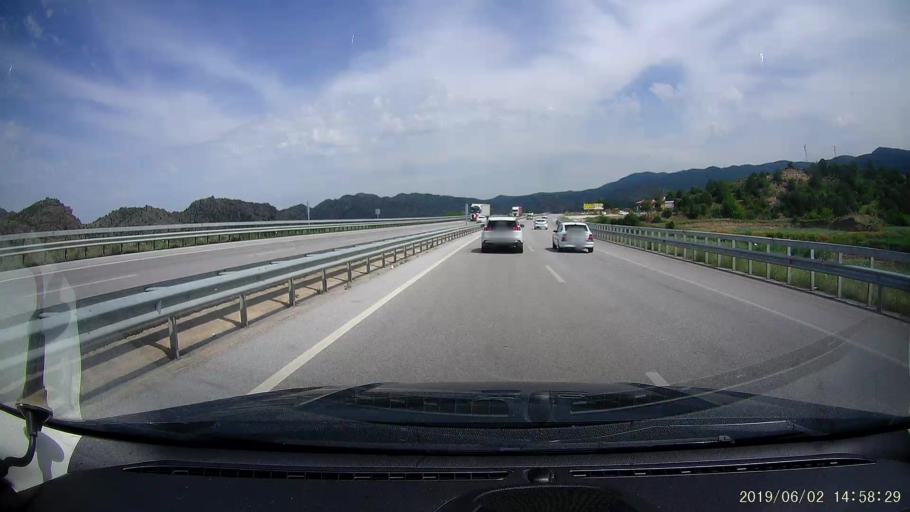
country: TR
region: Corum
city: Osmancik
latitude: 40.9815
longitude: 34.6767
